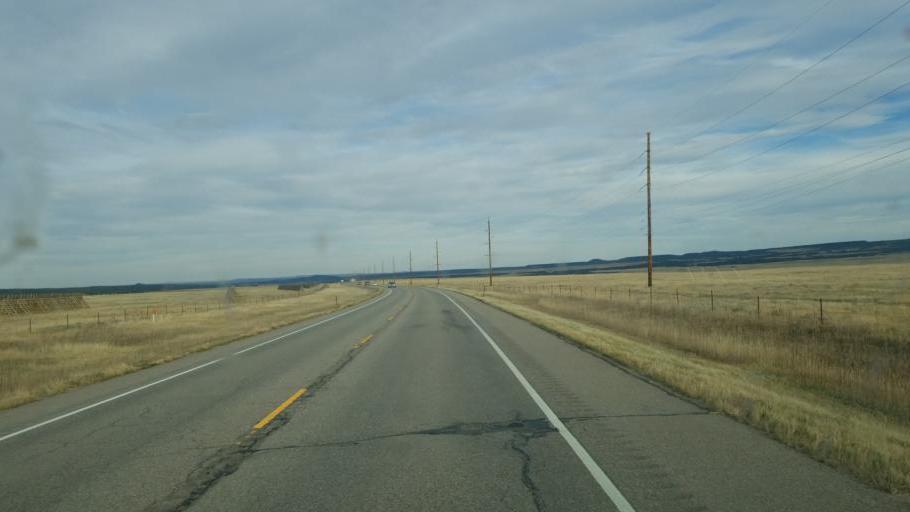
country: US
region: Colorado
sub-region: Huerfano County
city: Walsenburg
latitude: 37.5443
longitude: -105.0062
